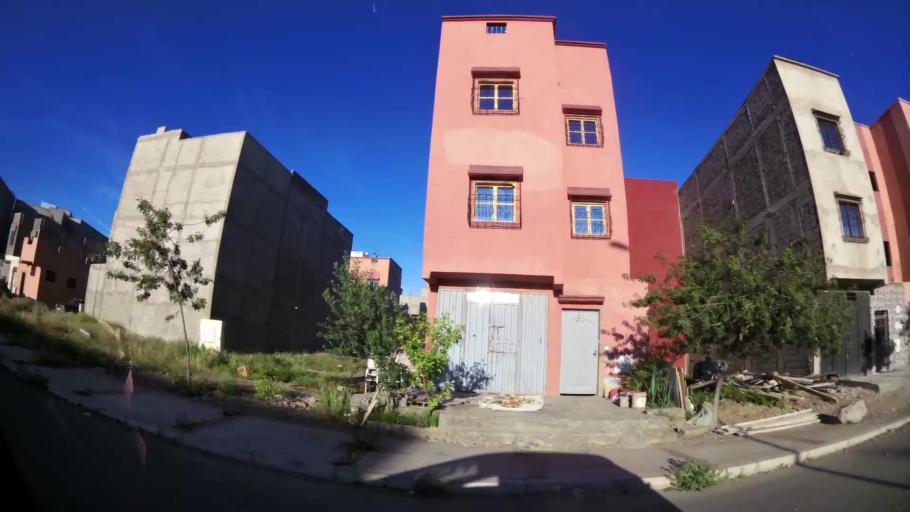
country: MA
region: Marrakech-Tensift-Al Haouz
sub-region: Marrakech
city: Marrakesh
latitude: 31.7444
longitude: -8.1167
